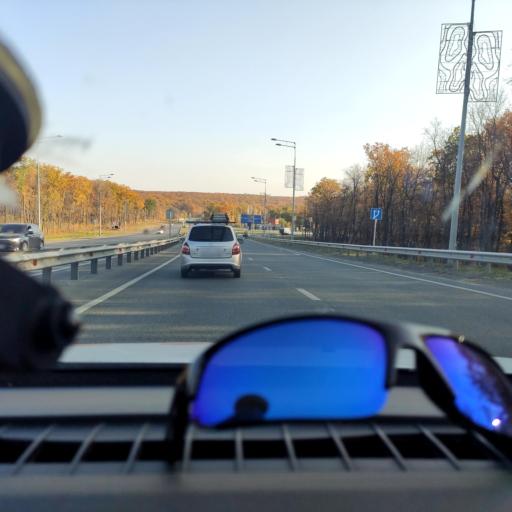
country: RU
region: Samara
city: Petra-Dubrava
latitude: 53.3107
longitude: 50.2325
